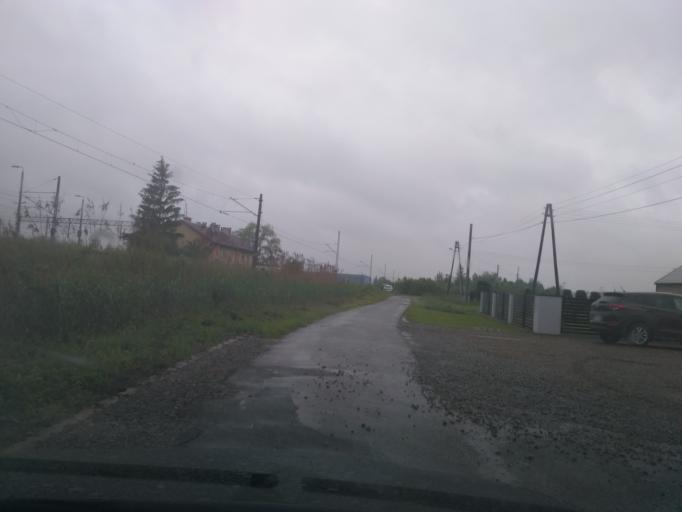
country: PL
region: Subcarpathian Voivodeship
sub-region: Powiat jasielski
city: Jaslo
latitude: 49.7464
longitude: 21.5189
